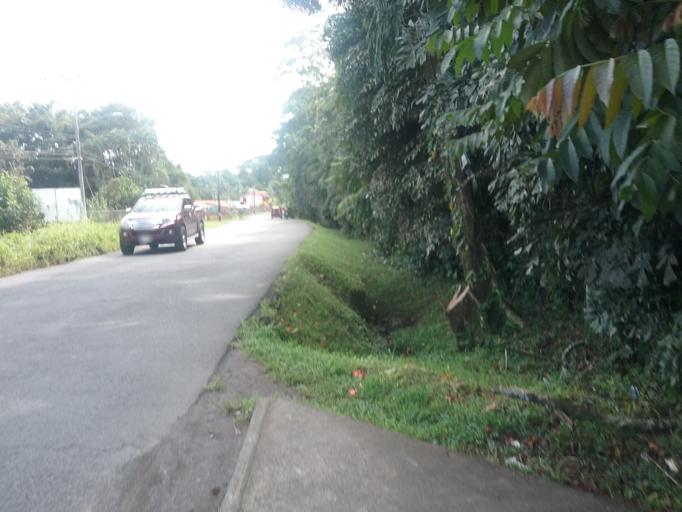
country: CR
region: Limon
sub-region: Canton de Pococi
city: Guapiles
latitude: 10.3203
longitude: -83.9132
